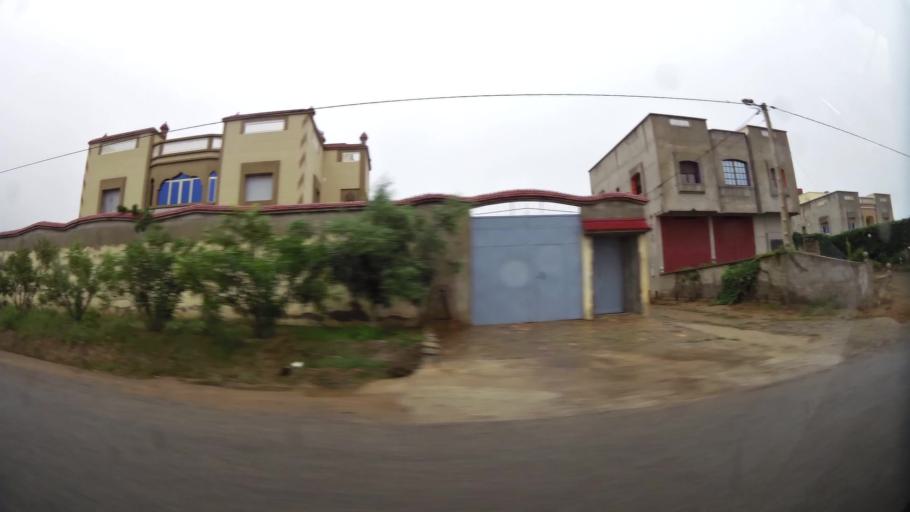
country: MA
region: Oriental
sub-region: Nador
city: Boudinar
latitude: 35.1249
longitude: -3.5773
